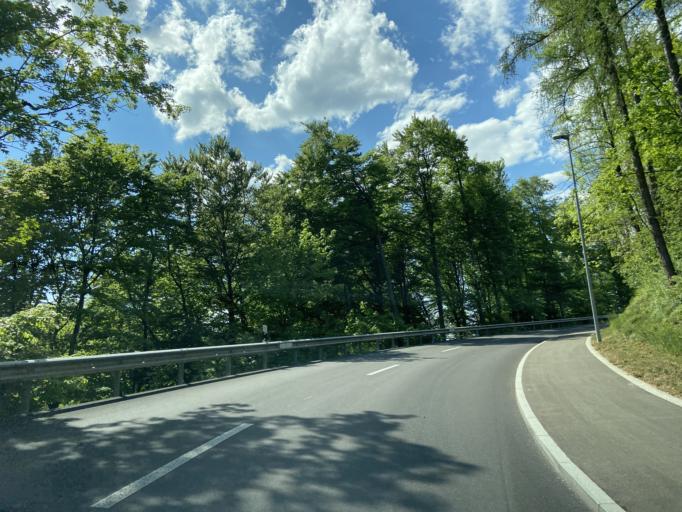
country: CH
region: Zurich
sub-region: Bezirk Winterthur
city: Pfungen
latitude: 47.5216
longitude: 8.6311
